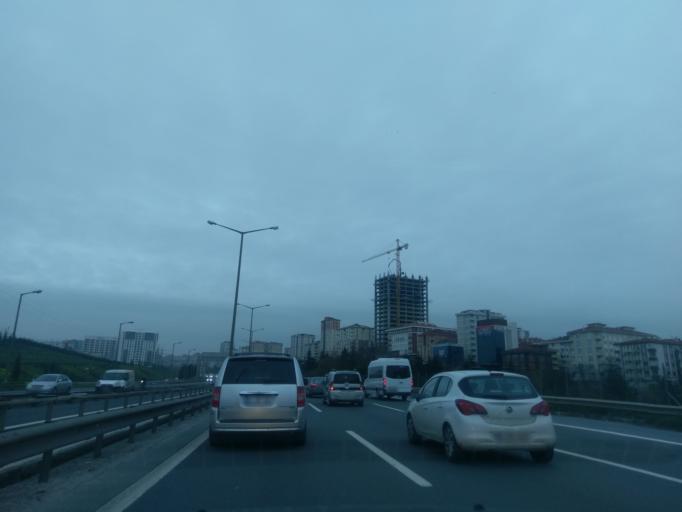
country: TR
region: Istanbul
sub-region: Atasehir
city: Atasehir
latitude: 40.9991
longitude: 29.1187
